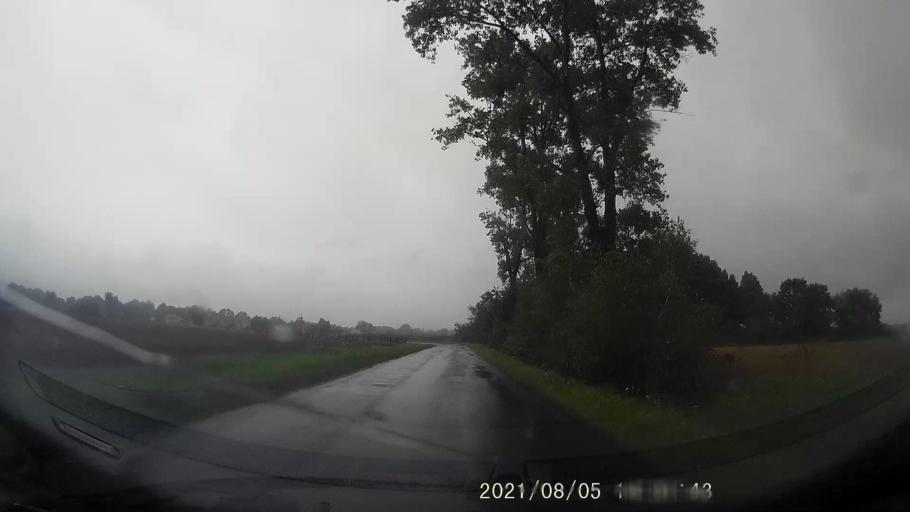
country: PL
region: Opole Voivodeship
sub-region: Powiat nyski
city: Korfantow
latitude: 50.4724
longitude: 17.5545
